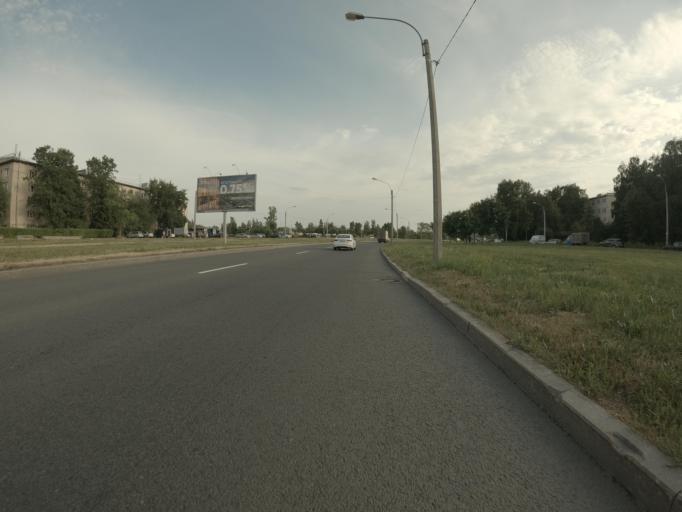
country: RU
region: Leningrad
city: Rybatskoye
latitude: 59.8829
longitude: 30.4882
